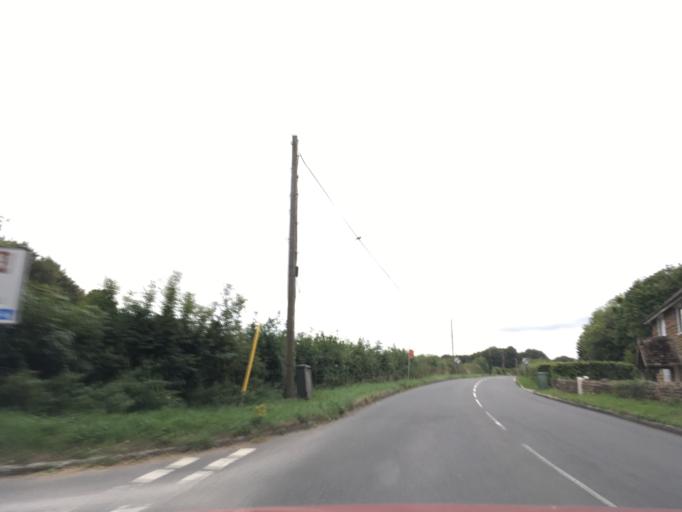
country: GB
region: England
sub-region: Wiltshire
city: Bremhill
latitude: 51.4130
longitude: -2.0534
